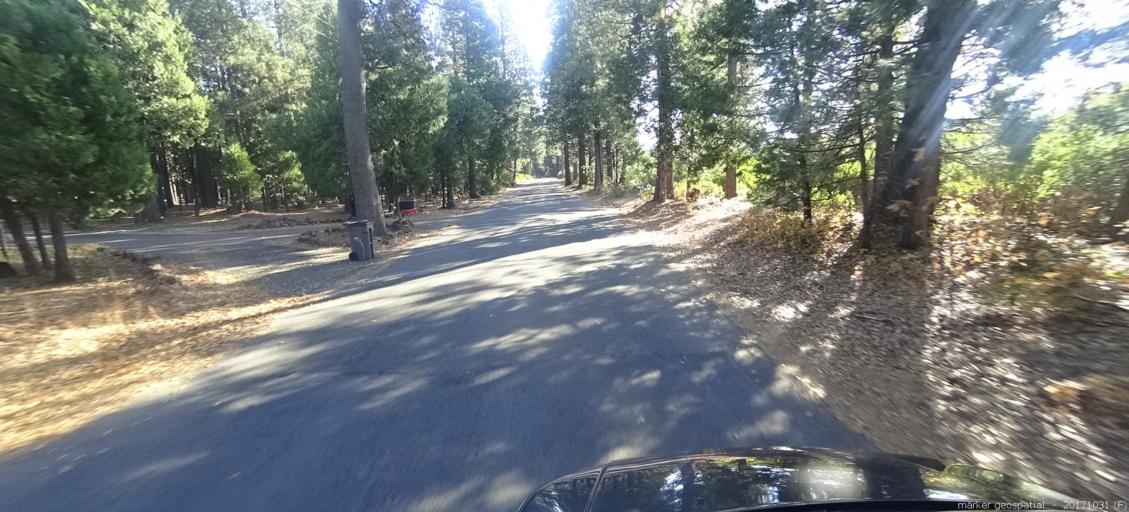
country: US
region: California
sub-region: Shasta County
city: Shingletown
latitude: 40.5191
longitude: -121.8354
